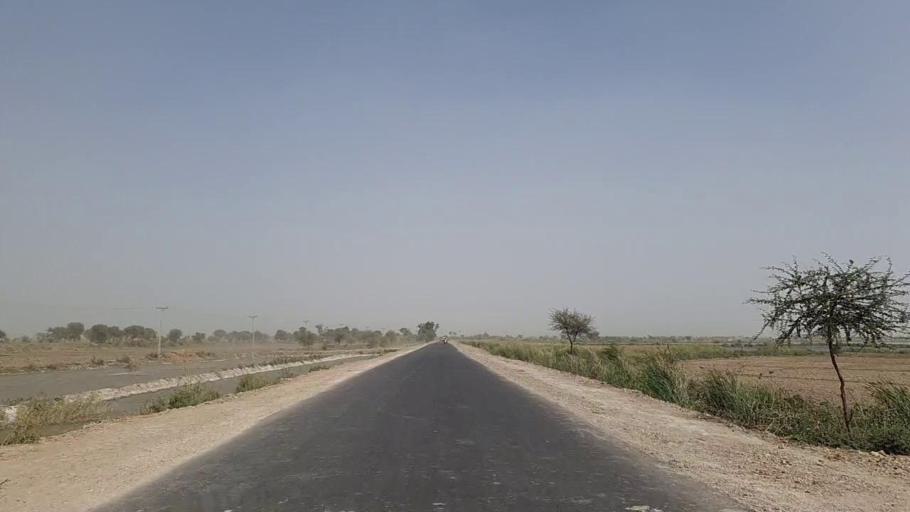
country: PK
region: Sindh
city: Tando Bago
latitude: 24.8093
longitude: 68.9202
